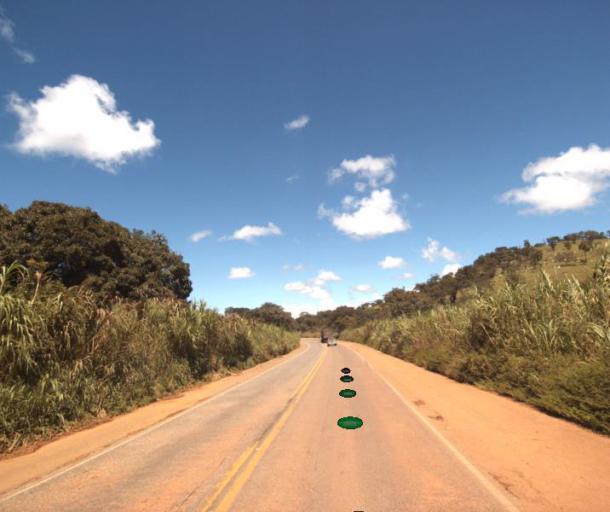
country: BR
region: Goias
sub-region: Anapolis
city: Anapolis
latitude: -16.1270
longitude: -49.0449
